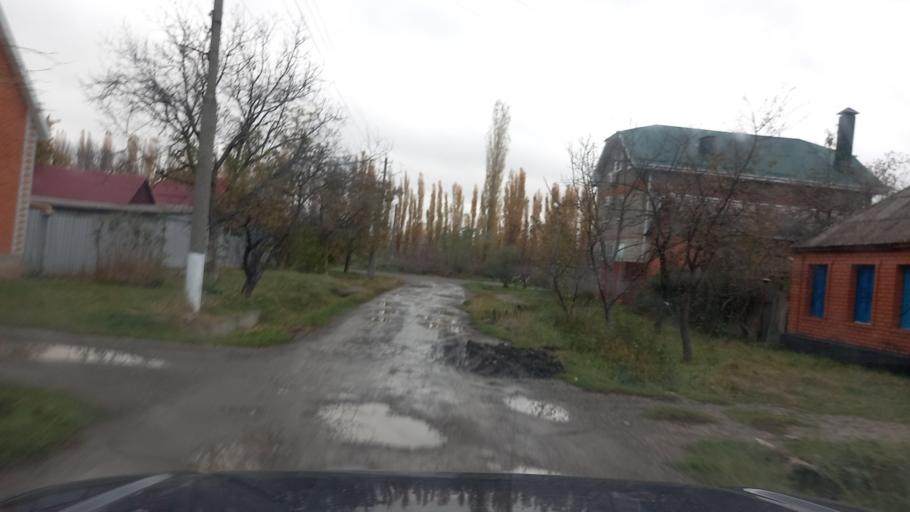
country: RU
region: Adygeya
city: Maykop
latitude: 44.6197
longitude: 40.1289
